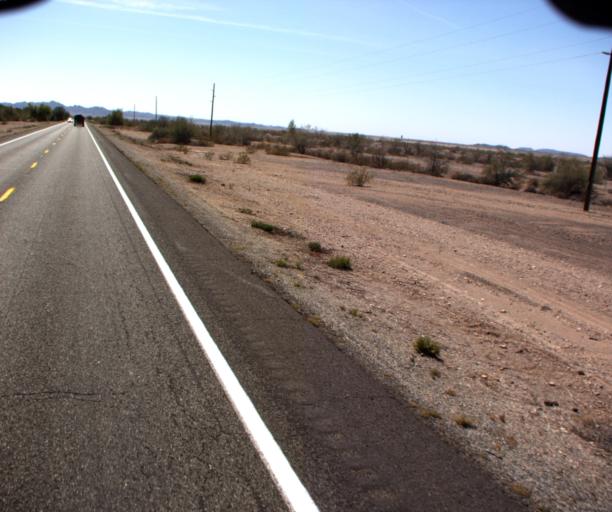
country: US
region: Arizona
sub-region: Yuma County
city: Fortuna Foothills
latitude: 32.8959
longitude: -114.3366
